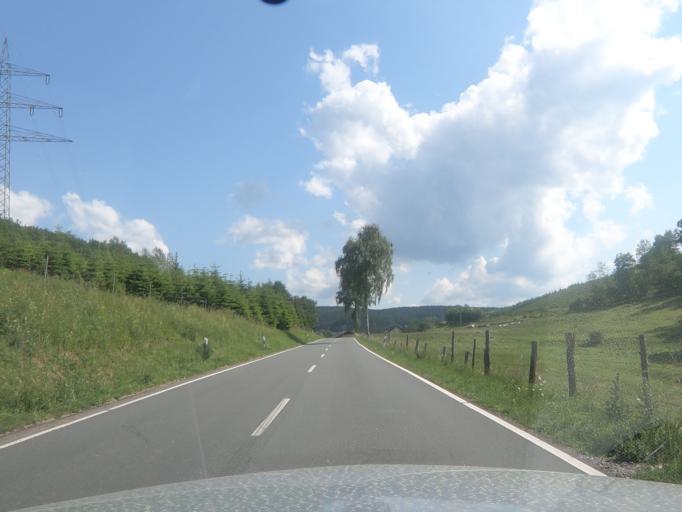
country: DE
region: North Rhine-Westphalia
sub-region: Regierungsbezirk Arnsberg
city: Attendorn
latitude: 51.0847
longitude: 7.9526
